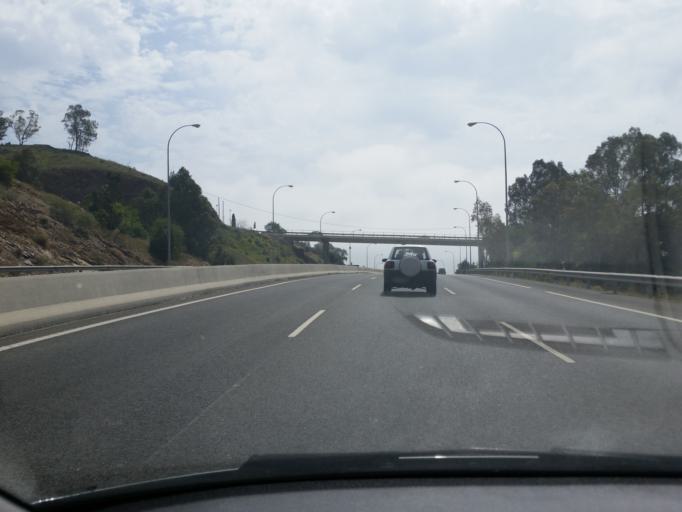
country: ES
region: Andalusia
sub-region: Provincia de Malaga
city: Malaga
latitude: 36.7477
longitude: -4.4096
